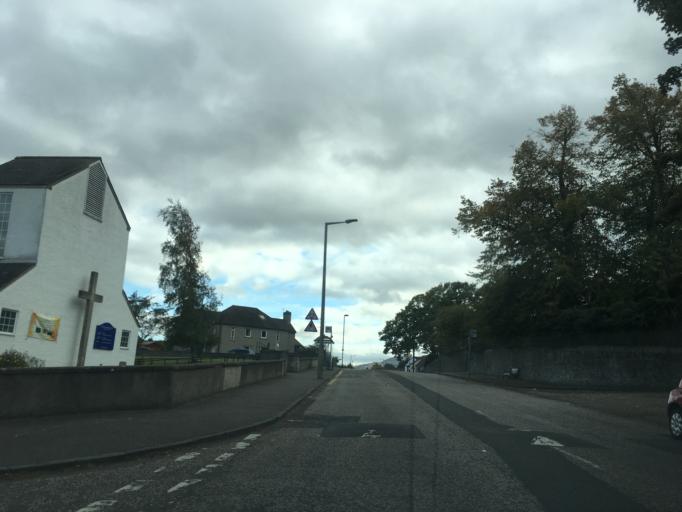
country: GB
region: Scotland
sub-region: Edinburgh
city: Edinburgh
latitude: 55.9654
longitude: -3.2497
